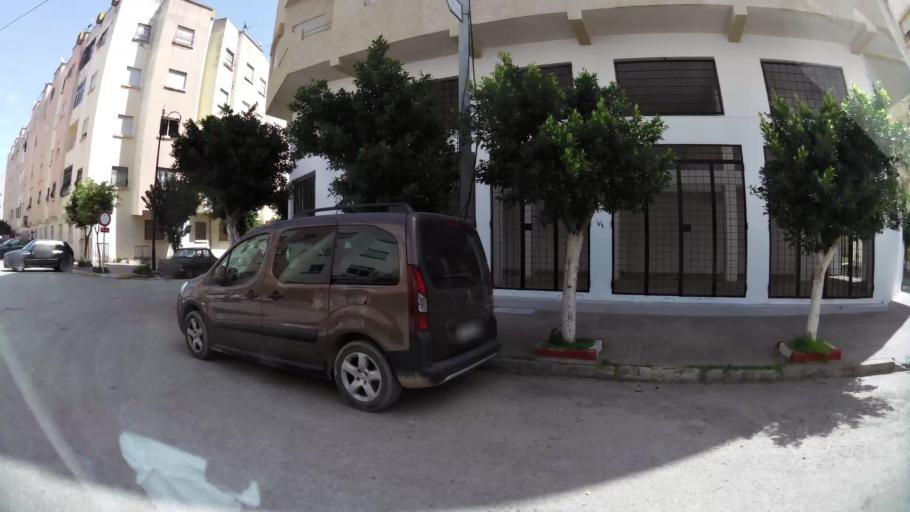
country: MA
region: Tanger-Tetouan
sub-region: Tanger-Assilah
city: Tangier
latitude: 35.7507
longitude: -5.8417
